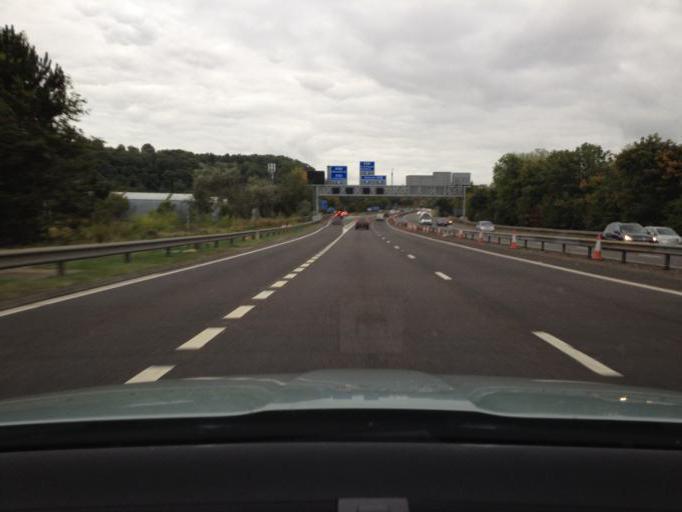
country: GB
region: Scotland
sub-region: Fife
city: Inverkeithing
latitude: 56.0400
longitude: -3.4064
